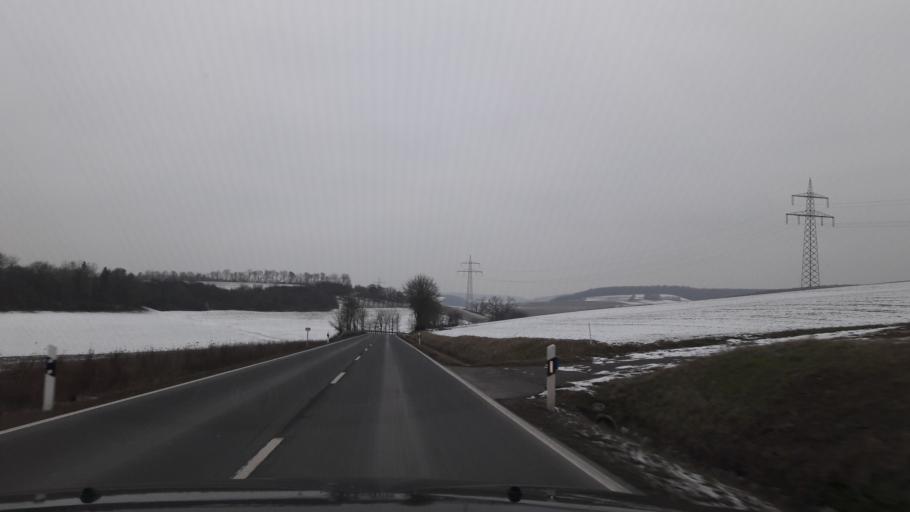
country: DE
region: Bavaria
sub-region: Regierungsbezirk Unterfranken
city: Waldbrunn
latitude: 49.7655
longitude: 9.7909
